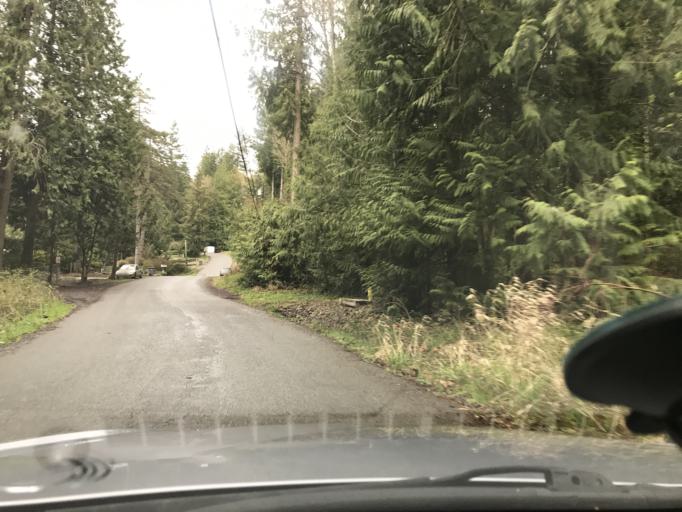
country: US
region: Washington
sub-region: King County
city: Ames Lake
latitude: 47.6452
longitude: -121.9572
